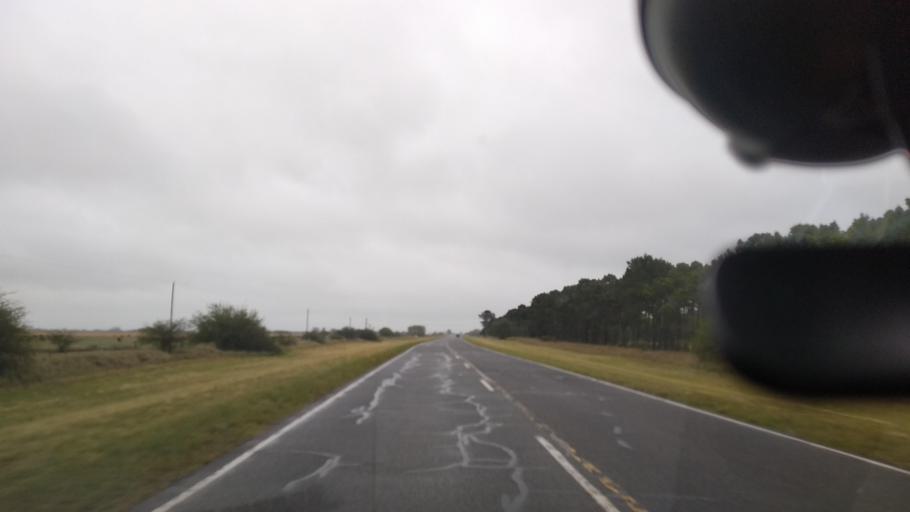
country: AR
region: Buenos Aires
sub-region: Partido de Dolores
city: Dolores
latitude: -36.0505
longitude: -57.4441
